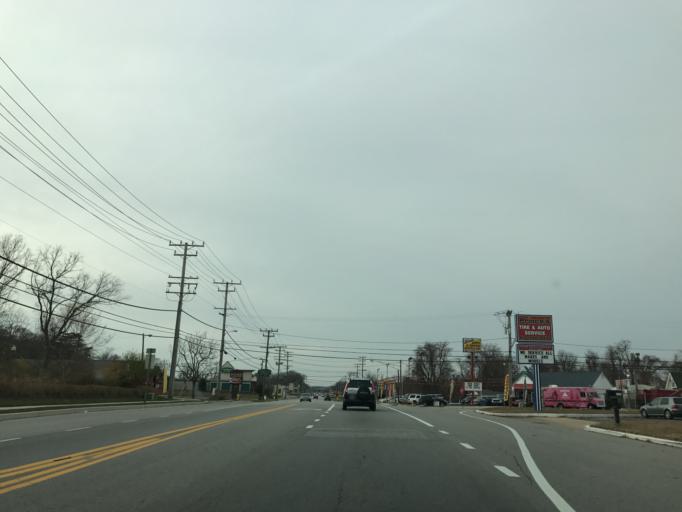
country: US
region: Maryland
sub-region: Anne Arundel County
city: Pasadena
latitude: 39.1331
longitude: -76.5784
